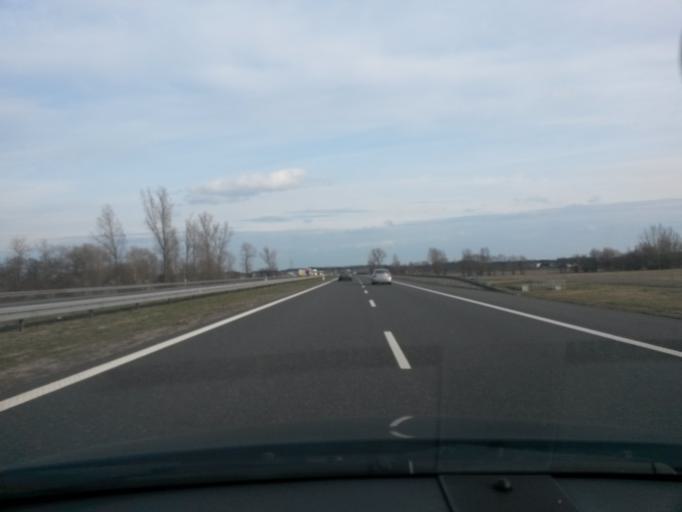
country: PL
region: Greater Poland Voivodeship
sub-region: Powiat kolski
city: Dabie
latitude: 52.0458
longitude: 18.8549
